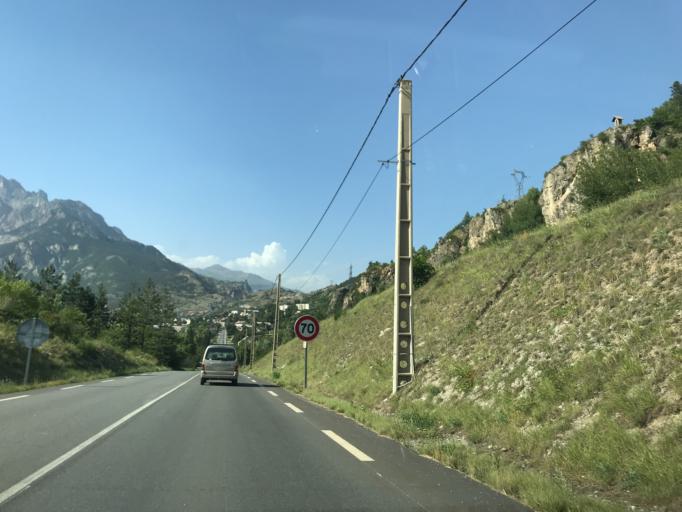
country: FR
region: Provence-Alpes-Cote d'Azur
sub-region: Departement des Hautes-Alpes
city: Saint-Martin-de-Queyrieres
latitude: 44.7850
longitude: 6.5608
